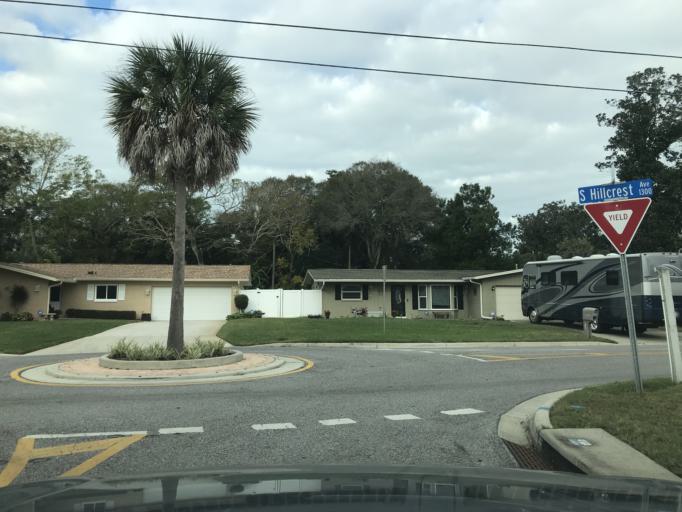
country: US
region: Florida
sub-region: Pinellas County
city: Clearwater
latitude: 27.9462
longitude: -82.7804
